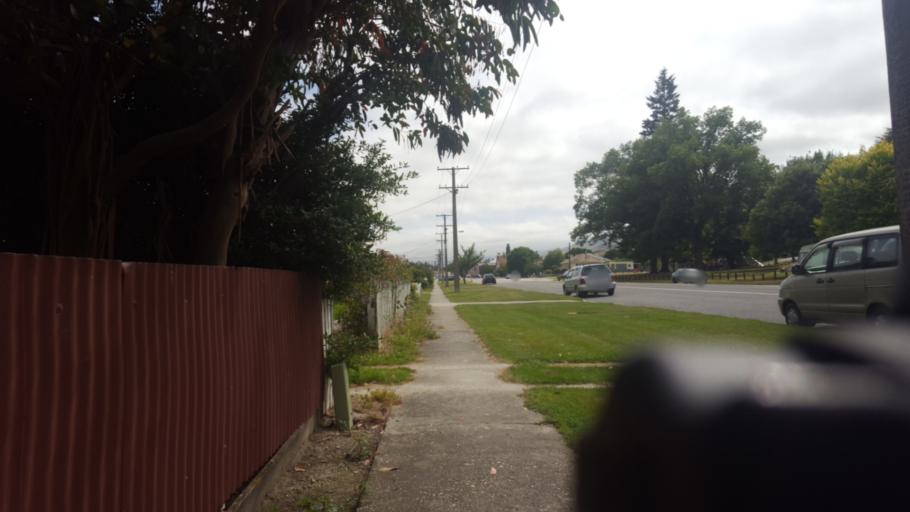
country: NZ
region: Otago
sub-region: Queenstown-Lakes District
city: Kingston
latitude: -45.5454
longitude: 169.3132
